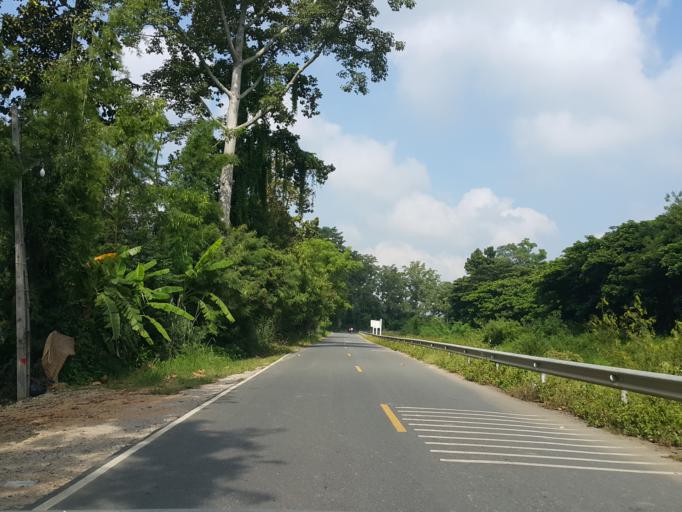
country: TH
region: Chiang Mai
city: San Sai
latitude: 18.9182
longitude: 99.0035
